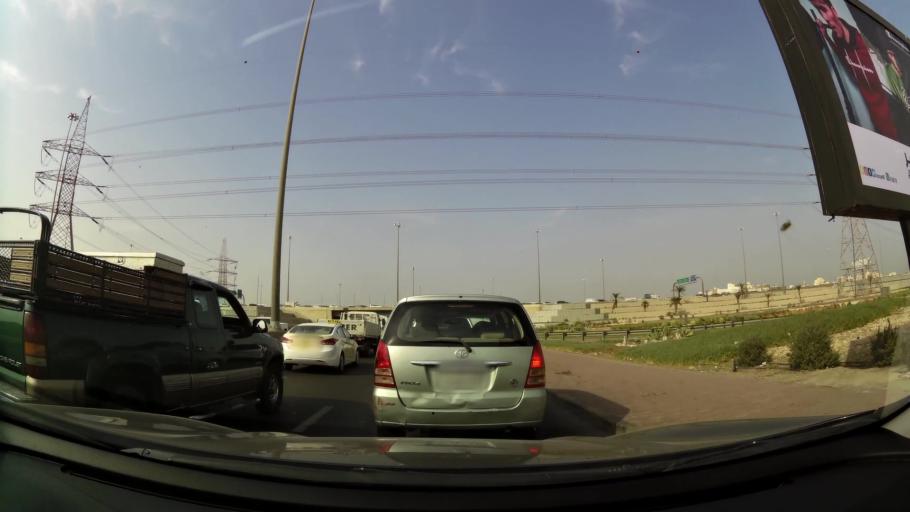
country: KW
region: Al Farwaniyah
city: Al Farwaniyah
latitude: 29.3013
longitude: 47.9640
